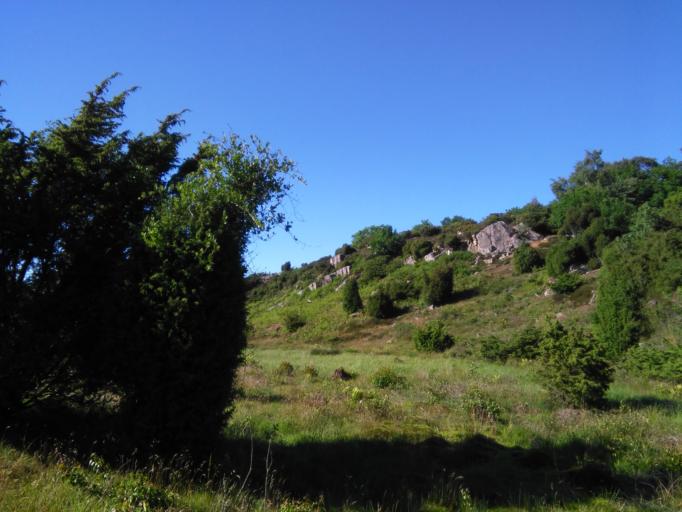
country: DK
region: Capital Region
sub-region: Bornholm Kommune
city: Ronne
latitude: 55.2598
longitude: 14.7689
